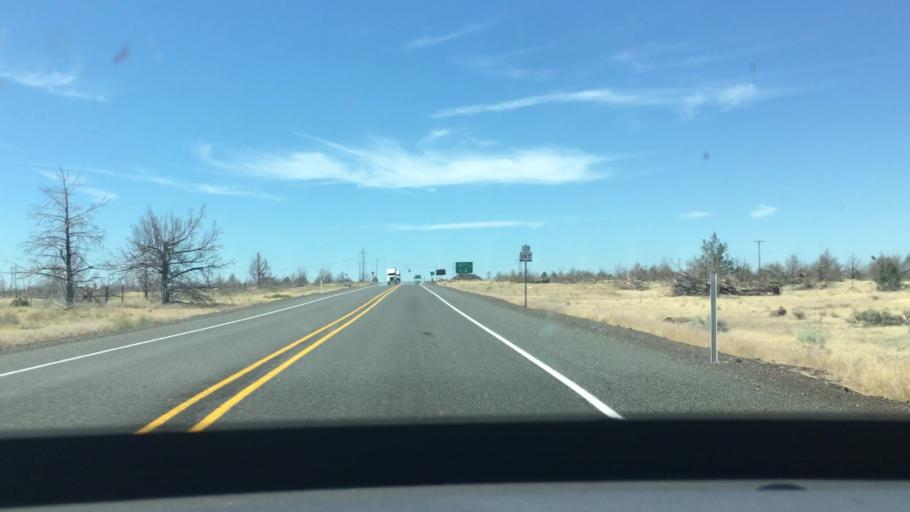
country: US
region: Oregon
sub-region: Jefferson County
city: Madras
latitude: 44.9155
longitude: -120.9426
